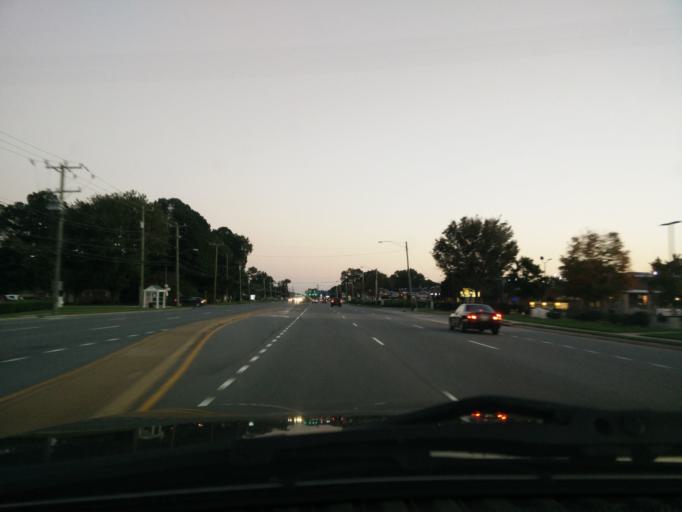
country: US
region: Virginia
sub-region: City of Chesapeake
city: Chesapeake
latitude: 36.7631
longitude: -76.2513
